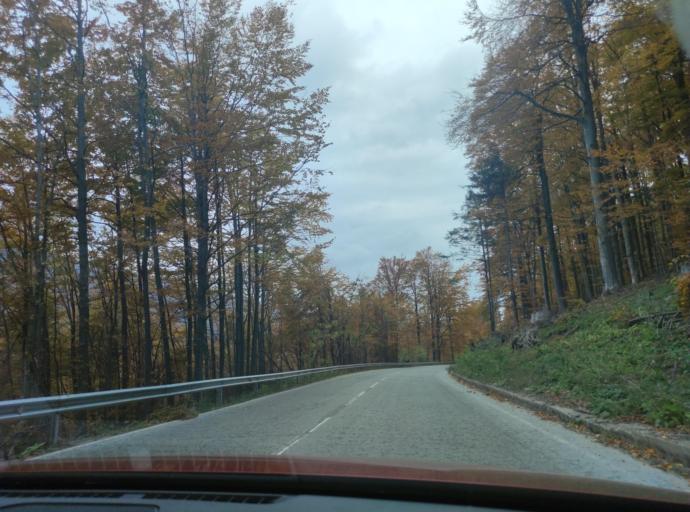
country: BG
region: Montana
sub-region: Obshtina Berkovitsa
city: Berkovitsa
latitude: 43.1403
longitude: 23.1423
